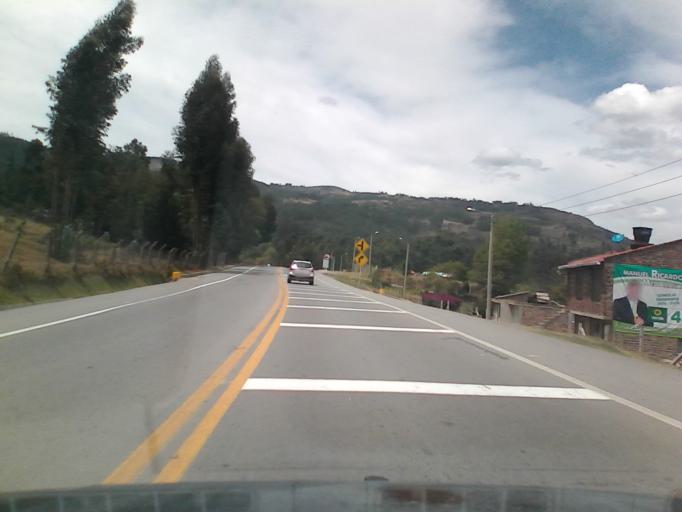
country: CO
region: Boyaca
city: Sogamoso
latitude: 5.7330
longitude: -72.9597
